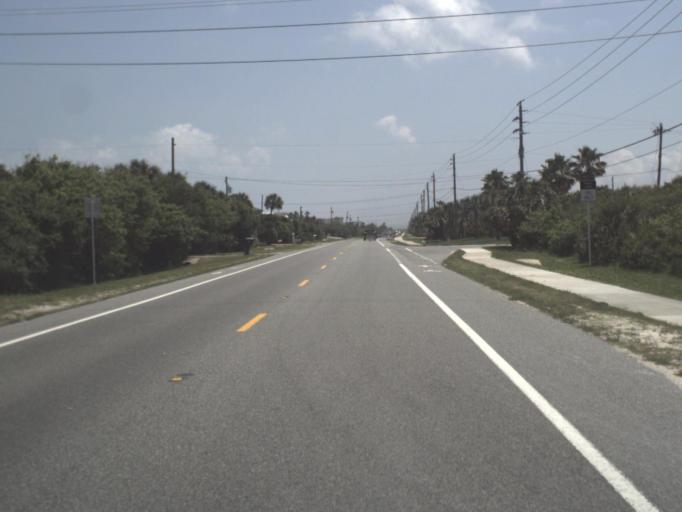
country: US
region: Florida
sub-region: Saint Johns County
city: Butler Beach
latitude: 29.7538
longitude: -81.2477
